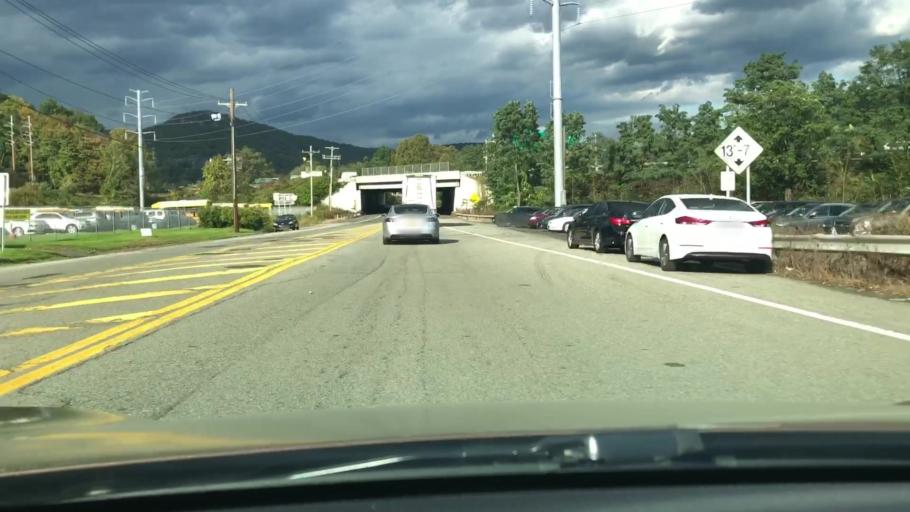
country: US
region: New York
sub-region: Rockland County
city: Suffern
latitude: 41.1323
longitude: -74.1693
